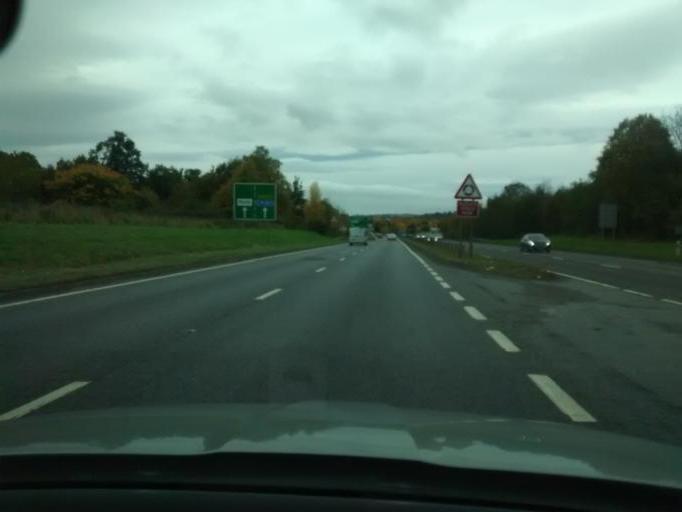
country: GB
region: Scotland
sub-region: Perth and Kinross
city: Luncarty
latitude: 56.4245
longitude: -3.4673
